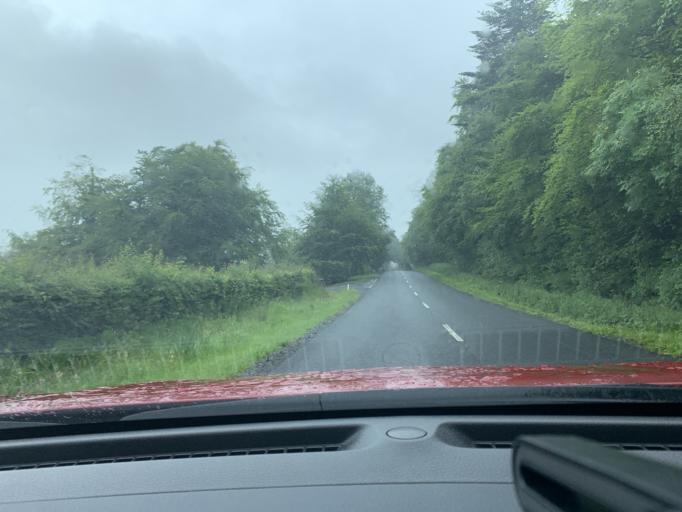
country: GB
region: Northern Ireland
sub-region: Fermanagh District
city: Enniskillen
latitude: 54.2617
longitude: -7.7387
